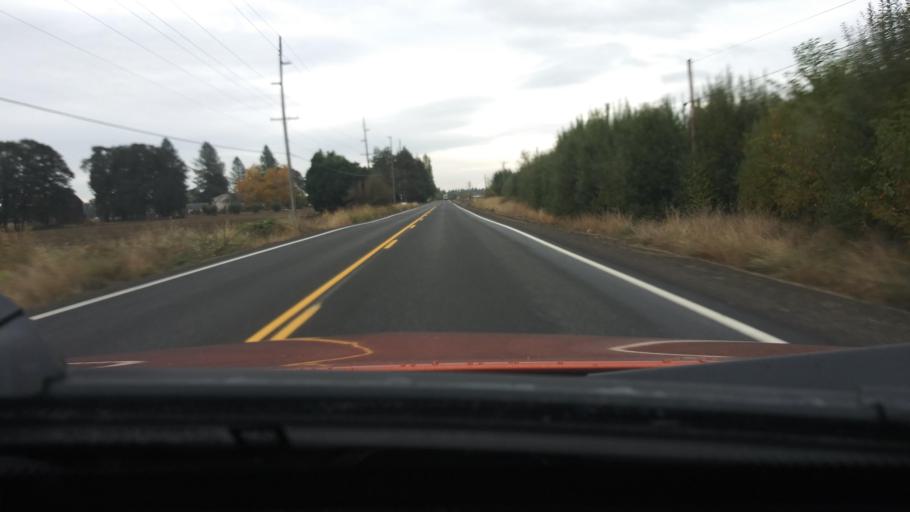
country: US
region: Oregon
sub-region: Washington County
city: Banks
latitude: 45.5813
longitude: -123.1134
